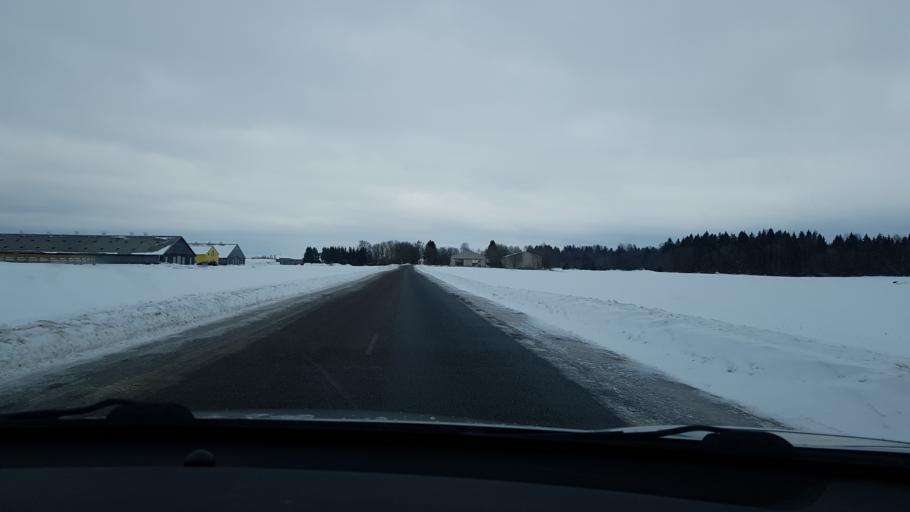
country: EE
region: Jaervamaa
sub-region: Koeru vald
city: Koeru
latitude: 58.9771
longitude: 25.9998
